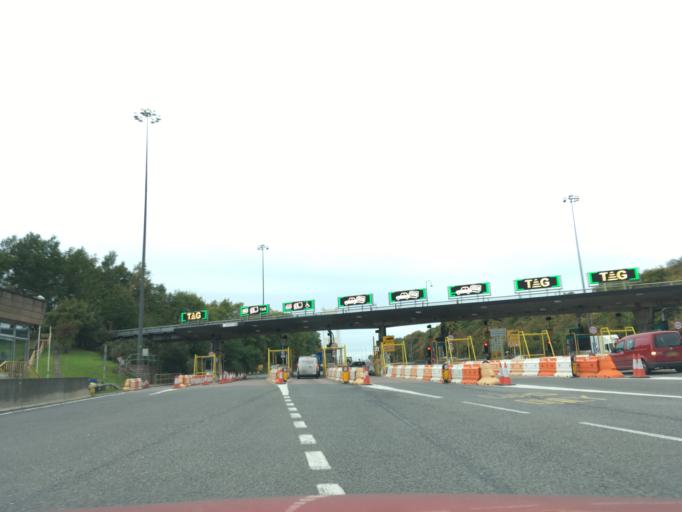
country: GB
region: England
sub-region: South Gloucestershire
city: Severn Beach
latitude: 51.6029
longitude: -2.6223
